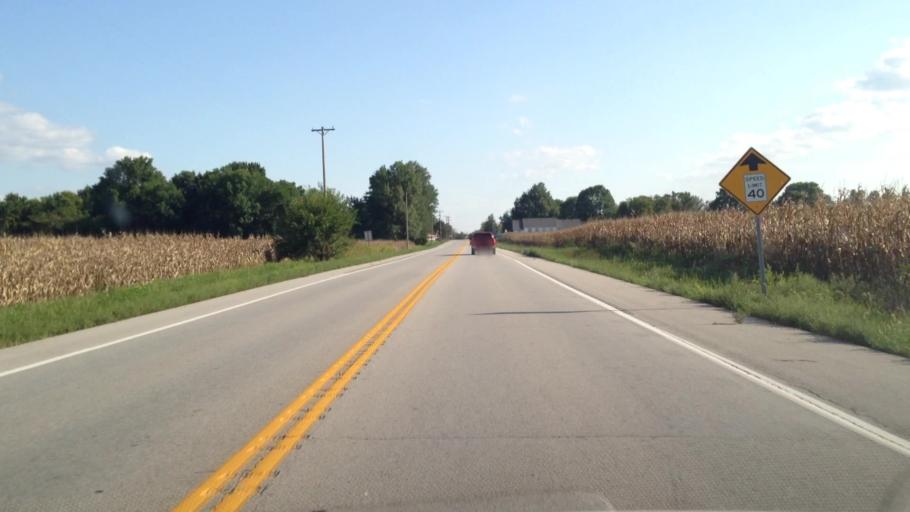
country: US
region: Missouri
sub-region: Jasper County
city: Carl Junction
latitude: 37.2790
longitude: -94.6009
